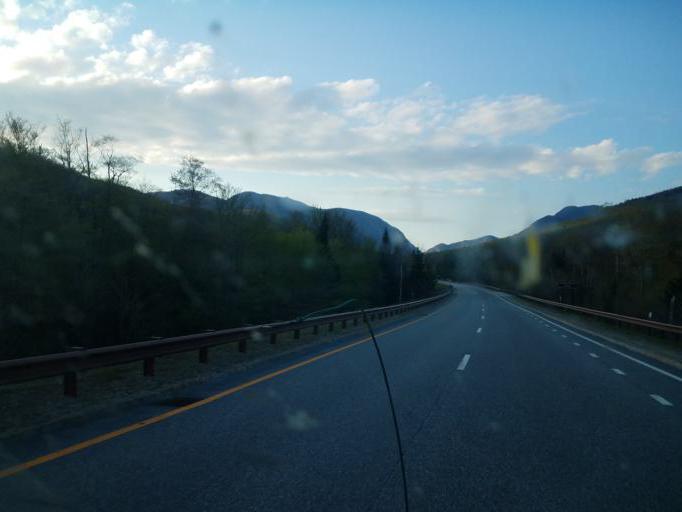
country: US
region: New Hampshire
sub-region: Grafton County
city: Woodstock
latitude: 44.1095
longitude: -71.6825
